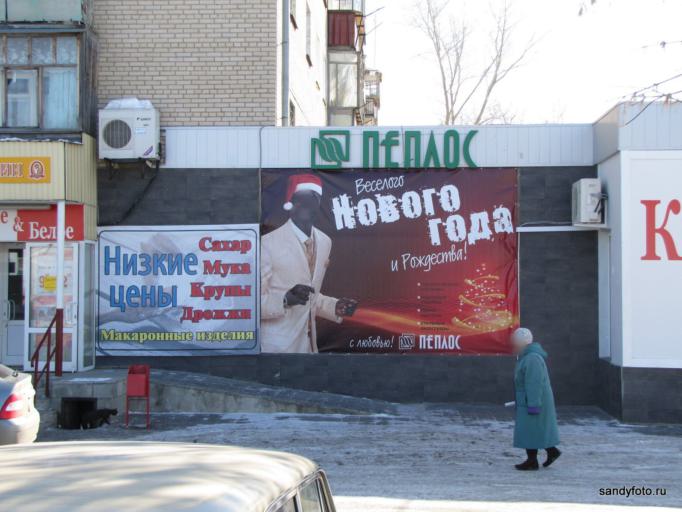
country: RU
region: Chelyabinsk
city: Troitsk
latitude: 54.0807
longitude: 61.5319
